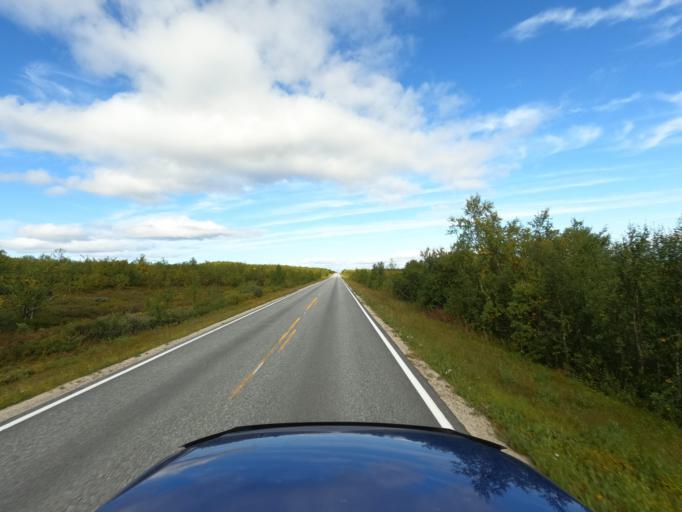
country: NO
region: Finnmark Fylke
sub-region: Karasjok
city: Karasjohka
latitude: 69.6479
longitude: 25.2805
